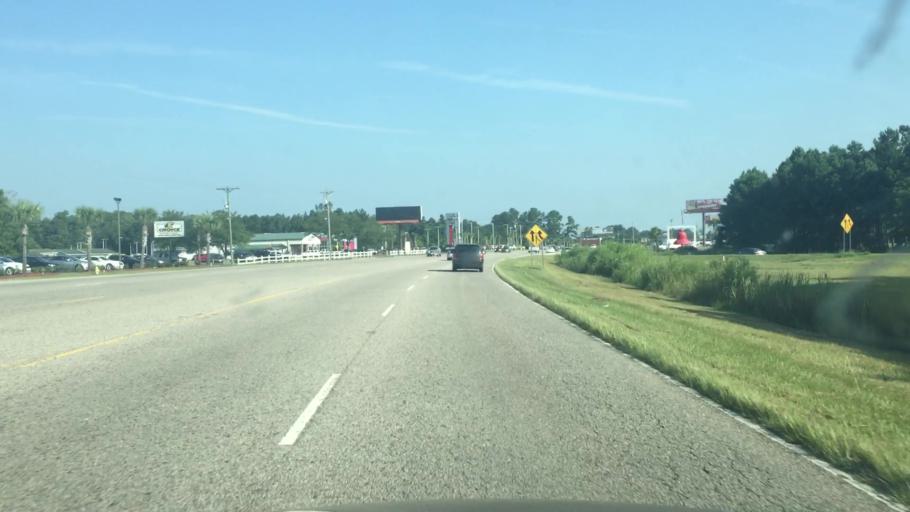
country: US
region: South Carolina
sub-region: Horry County
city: North Myrtle Beach
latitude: 33.8785
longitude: -78.6855
